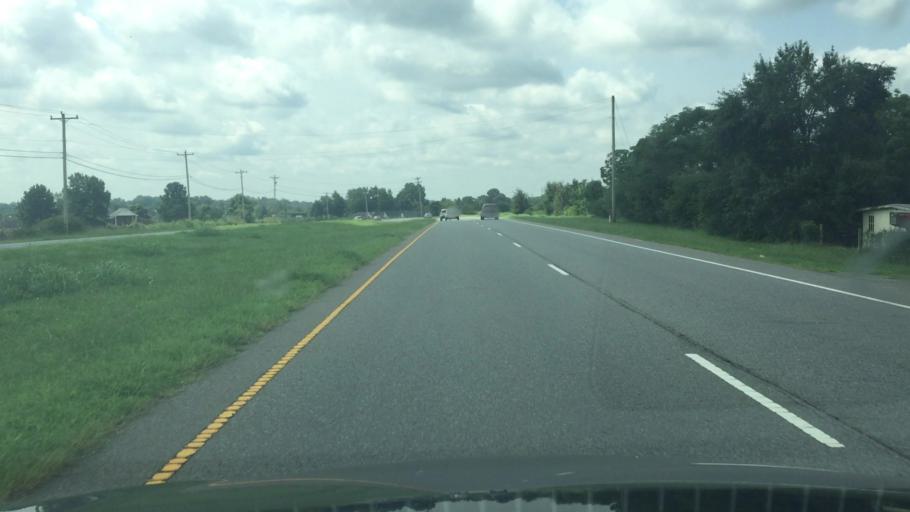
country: US
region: North Carolina
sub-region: Rowan County
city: Enochville
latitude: 35.4843
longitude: -80.6734
